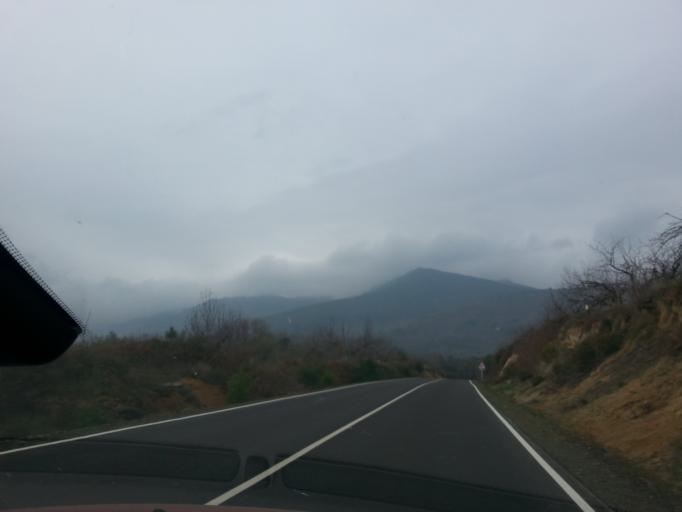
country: ES
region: Castille and Leon
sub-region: Provincia de Salamanca
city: Herguijuela de la Sierra
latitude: 40.4481
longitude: -6.0600
